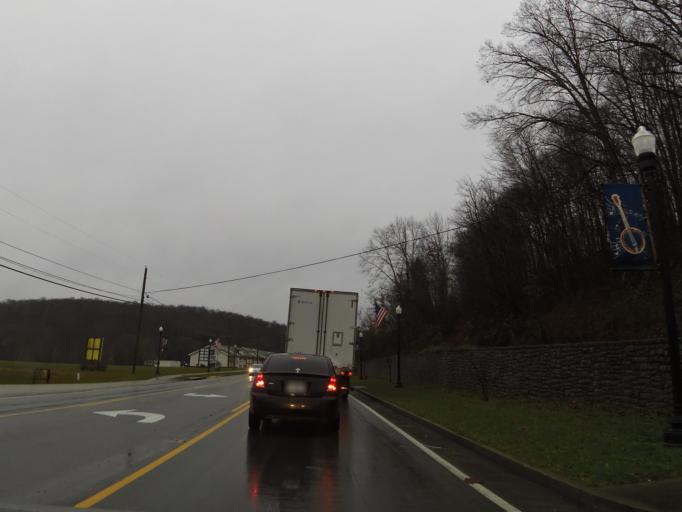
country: US
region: Kentucky
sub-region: Rockcastle County
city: Mount Vernon
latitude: 37.3845
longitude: -84.3309
